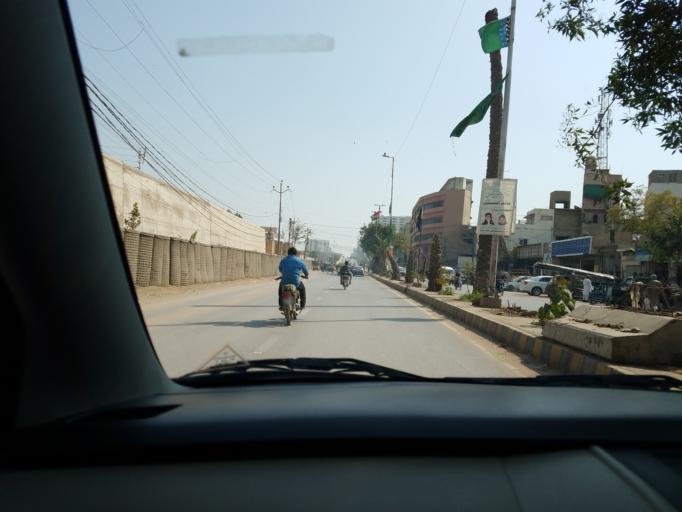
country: PK
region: Sindh
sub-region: Karachi District
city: Karachi
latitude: 24.8878
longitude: 67.0521
